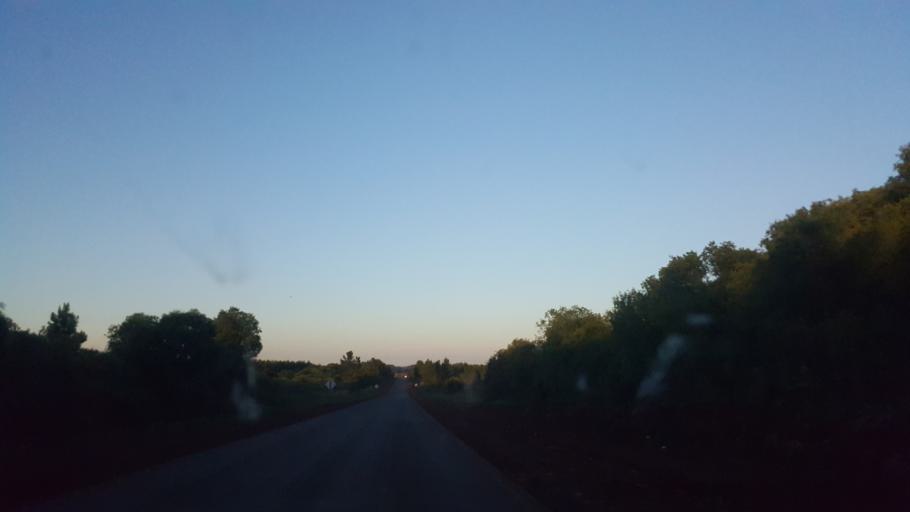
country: AR
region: Corrientes
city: Santo Tome
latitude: -28.3986
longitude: -55.9743
